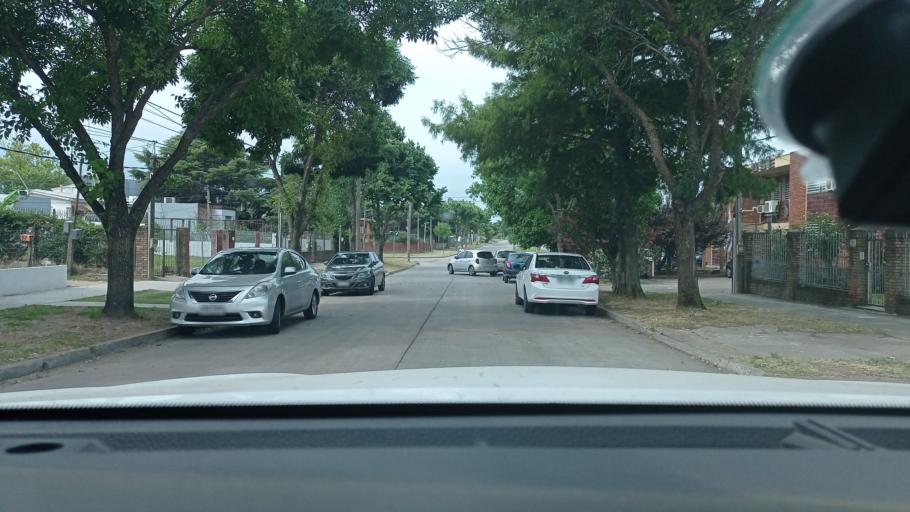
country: UY
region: Canelones
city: Paso de Carrasco
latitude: -34.8736
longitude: -56.0901
